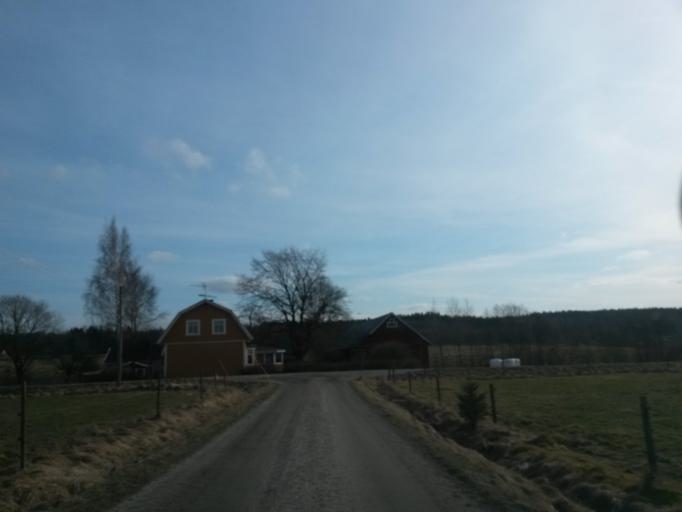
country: SE
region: Vaestra Goetaland
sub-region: Vargarda Kommun
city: Jonstorp
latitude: 57.9737
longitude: 12.6568
